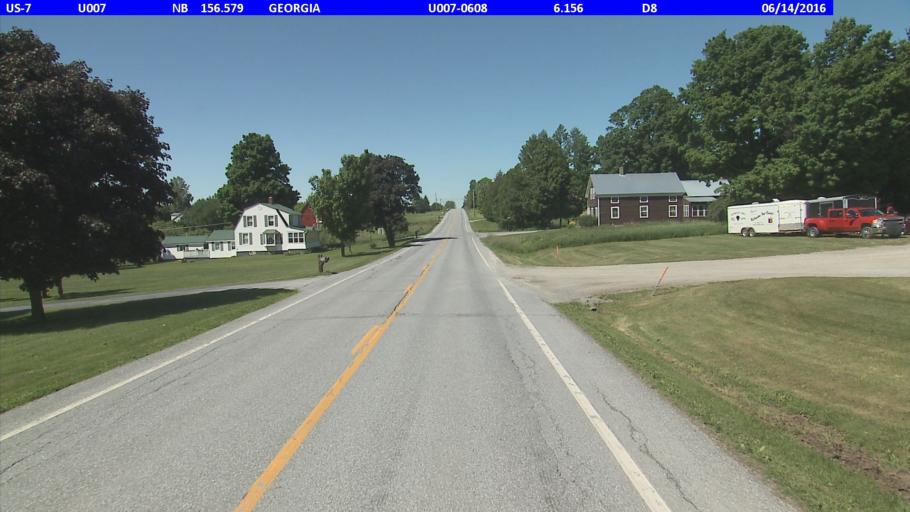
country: US
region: Vermont
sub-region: Franklin County
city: Saint Albans
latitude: 44.7597
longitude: -73.1101
